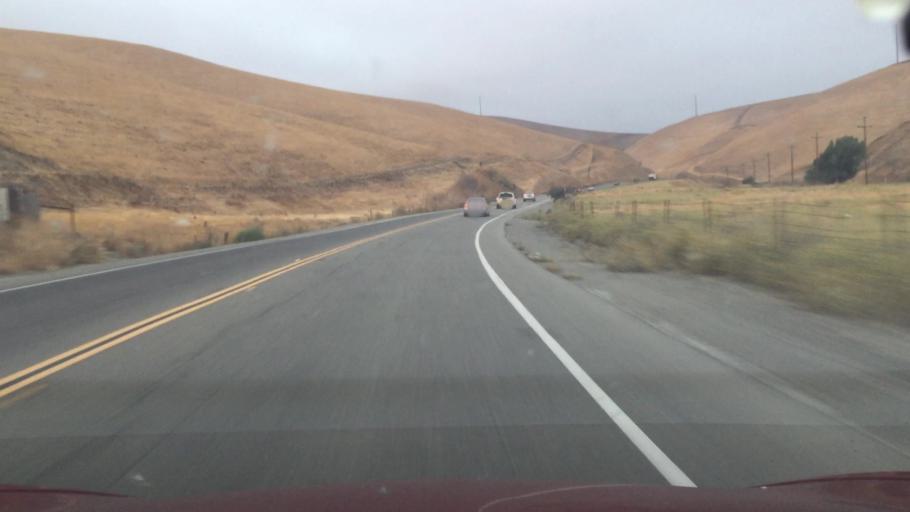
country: US
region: California
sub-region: Alameda County
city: Livermore
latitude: 37.7341
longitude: -121.6706
